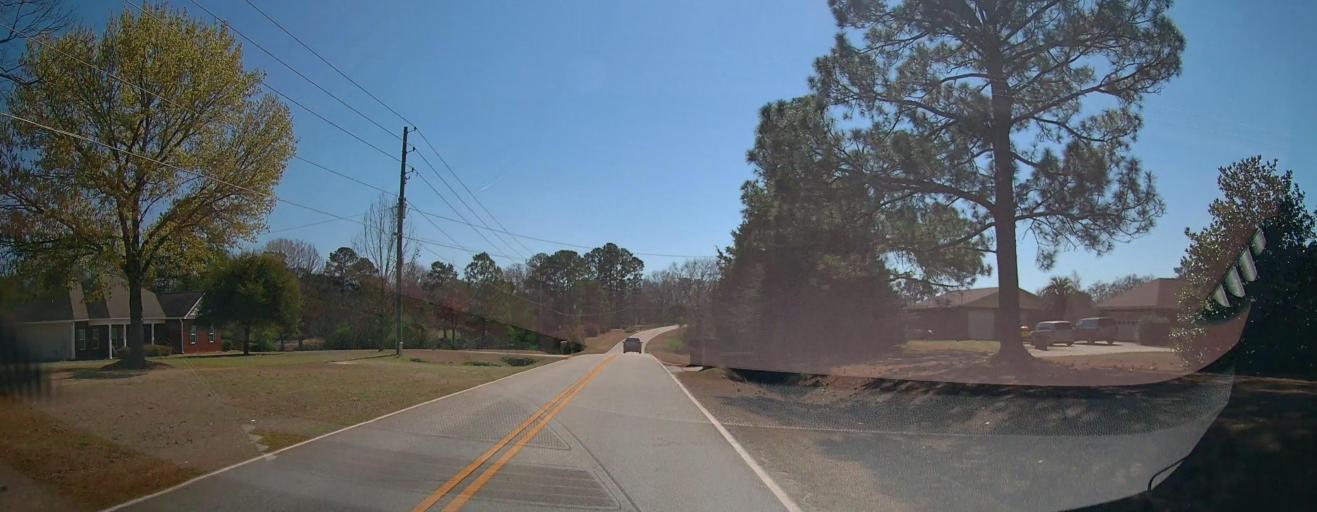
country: US
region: Georgia
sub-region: Houston County
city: Warner Robins
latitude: 32.5710
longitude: -83.6346
